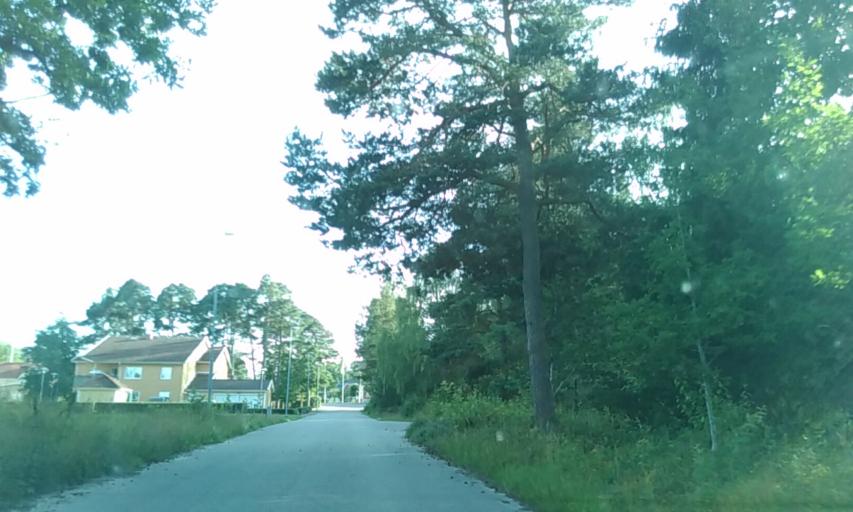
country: SE
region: Vaestra Goetaland
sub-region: Vara Kommun
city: Vara
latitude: 58.3272
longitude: 12.9252
